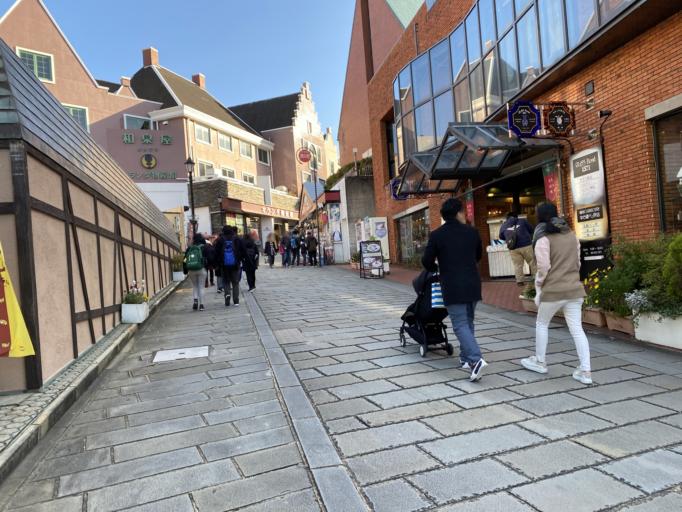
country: JP
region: Nagasaki
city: Nagasaki-shi
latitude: 32.7353
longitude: 129.8701
